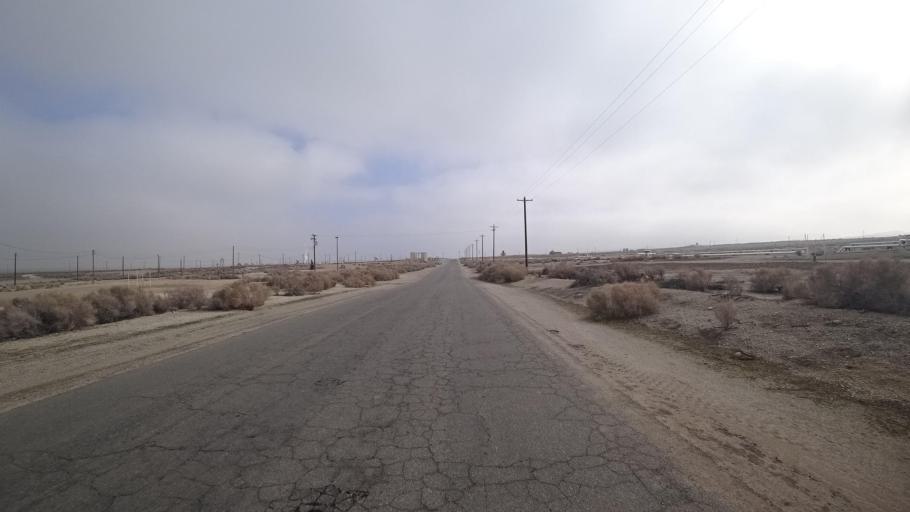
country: US
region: California
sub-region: Kern County
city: Maricopa
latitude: 35.0349
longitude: -119.3532
